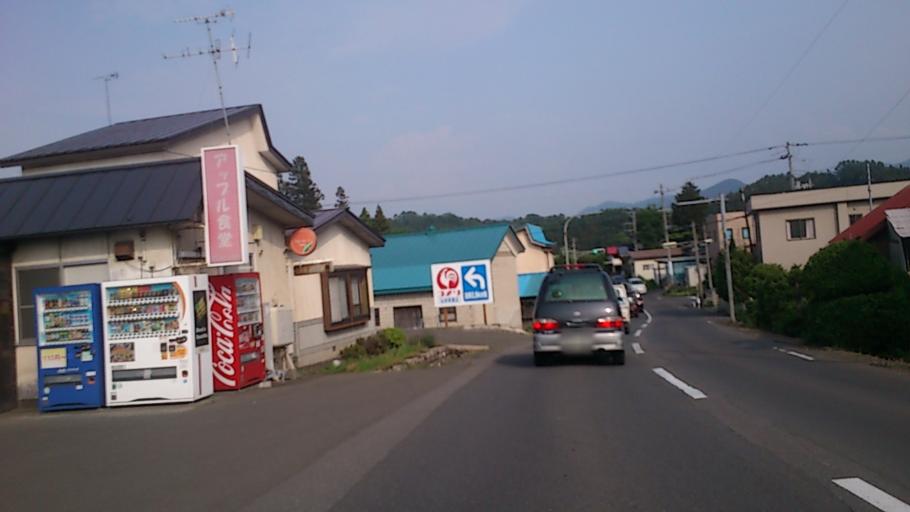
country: JP
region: Aomori
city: Hirosaki
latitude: 40.5633
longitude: 140.4390
